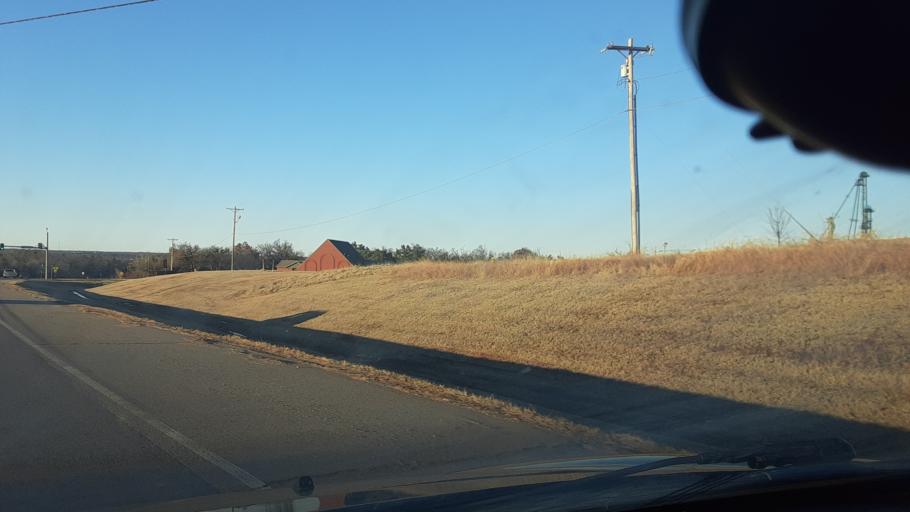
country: US
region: Oklahoma
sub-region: Logan County
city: Guthrie
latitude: 35.8269
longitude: -97.4230
